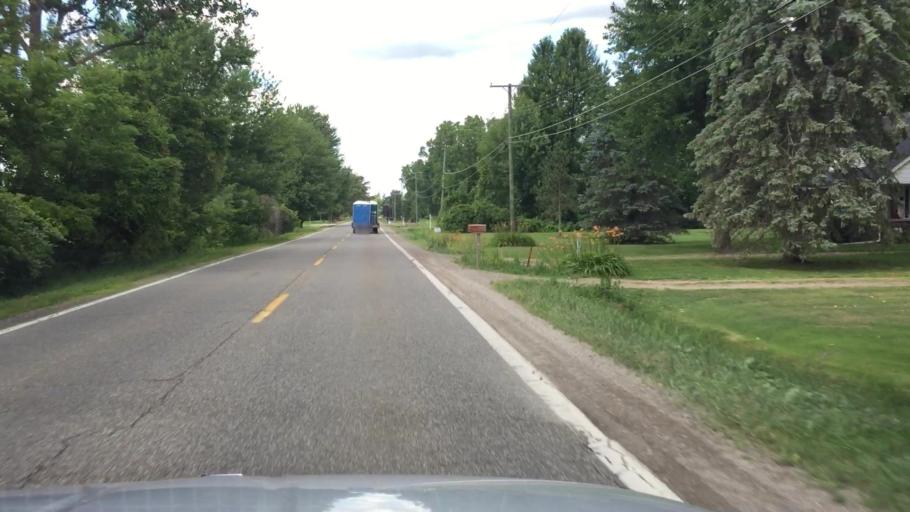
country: US
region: Michigan
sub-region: Macomb County
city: Armada
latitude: 42.8678
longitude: -82.9450
